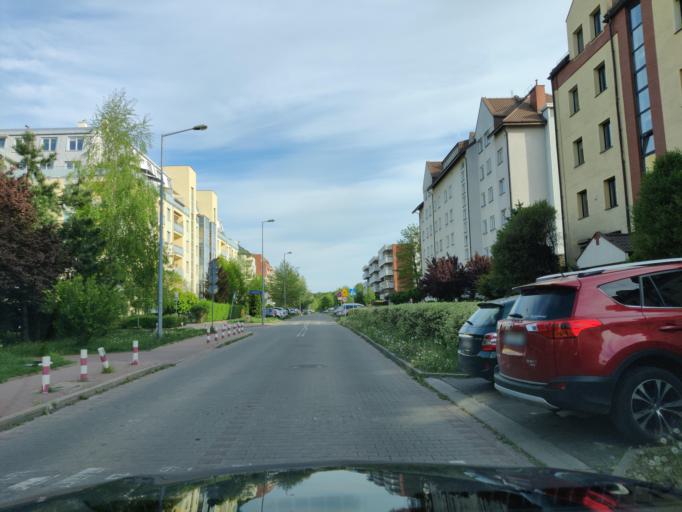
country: PL
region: Masovian Voivodeship
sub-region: Warszawa
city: Kabaty
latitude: 52.1312
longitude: 21.0742
